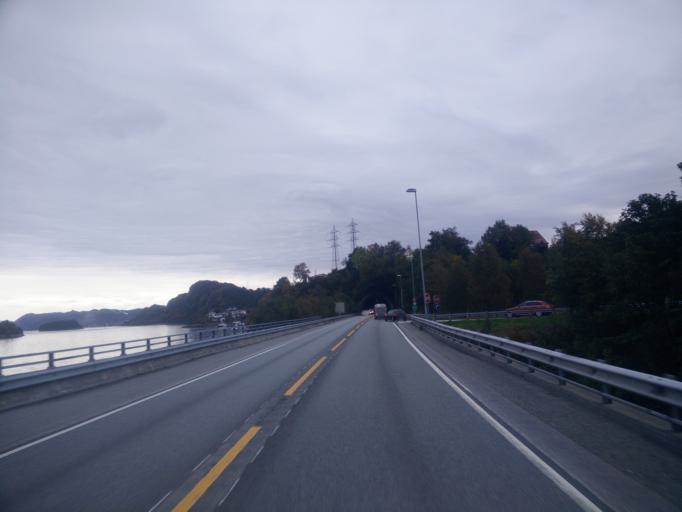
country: NO
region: More og Romsdal
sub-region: Sula
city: Langevag
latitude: 62.4704
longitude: 6.2427
